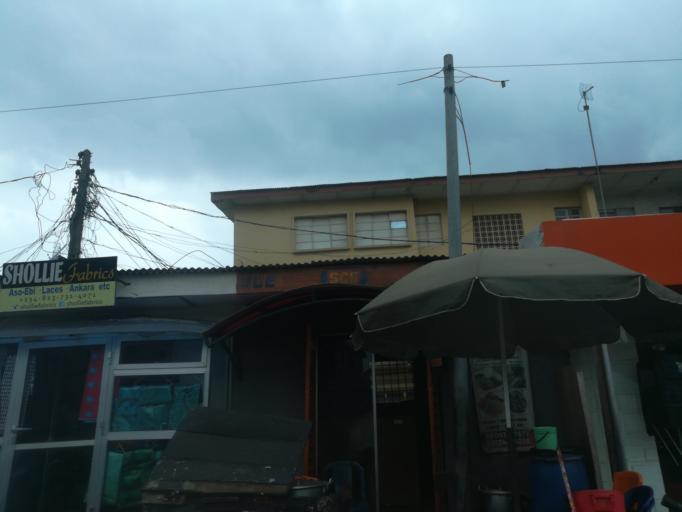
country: NG
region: Lagos
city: Ikeja
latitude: 6.6026
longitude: 3.3469
